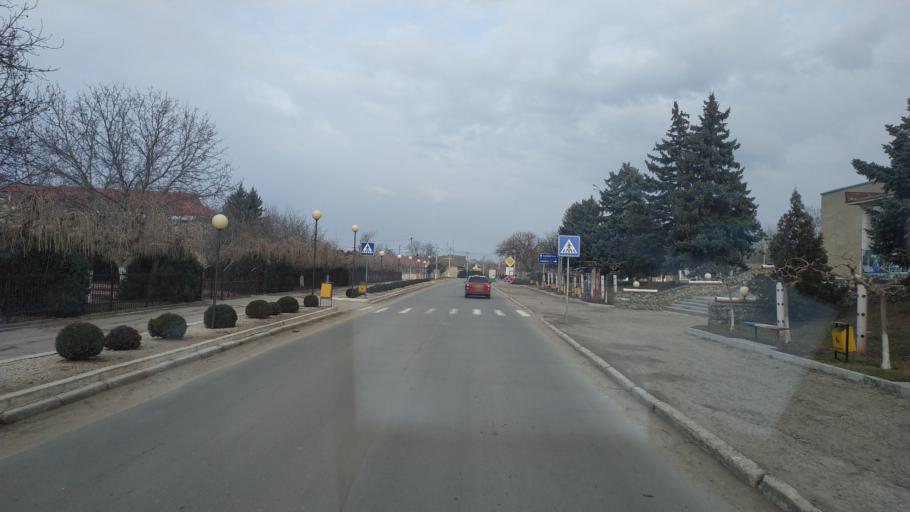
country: MD
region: Chisinau
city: Singera
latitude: 46.9627
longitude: 29.0566
